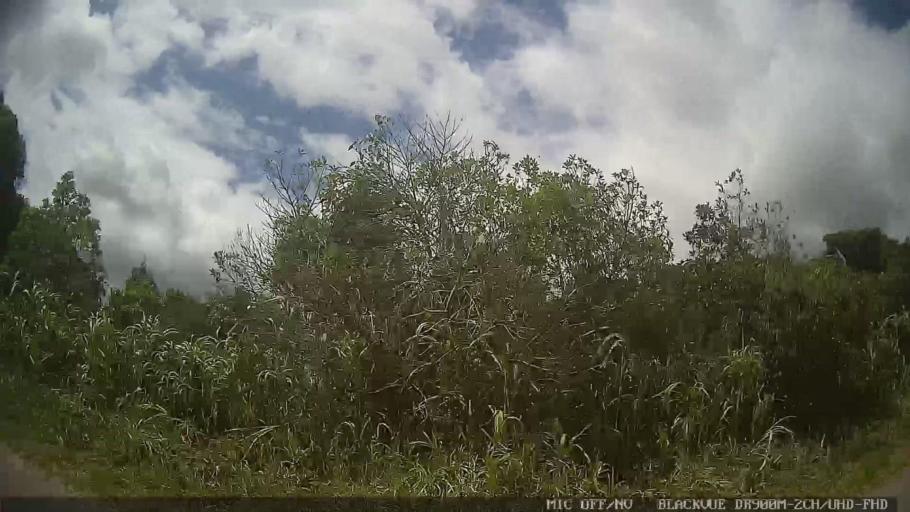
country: BR
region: Sao Paulo
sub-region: Braganca Paulista
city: Braganca Paulista
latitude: -22.8069
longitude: -46.5281
